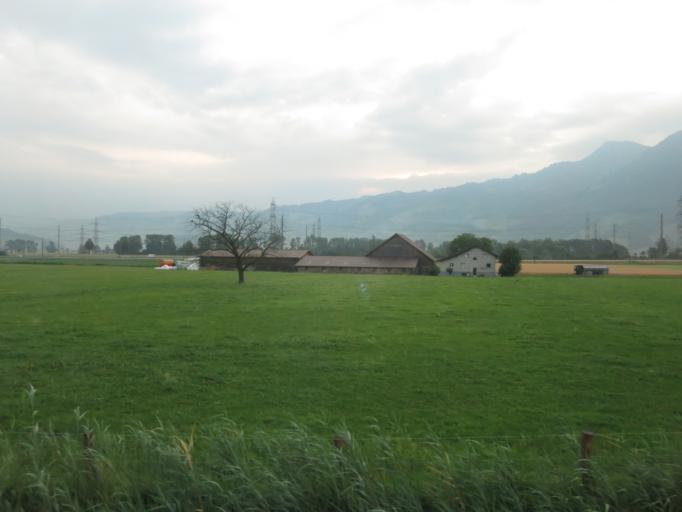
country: CH
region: Glarus
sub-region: Glarus
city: Bilten
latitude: 47.1562
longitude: 9.0224
